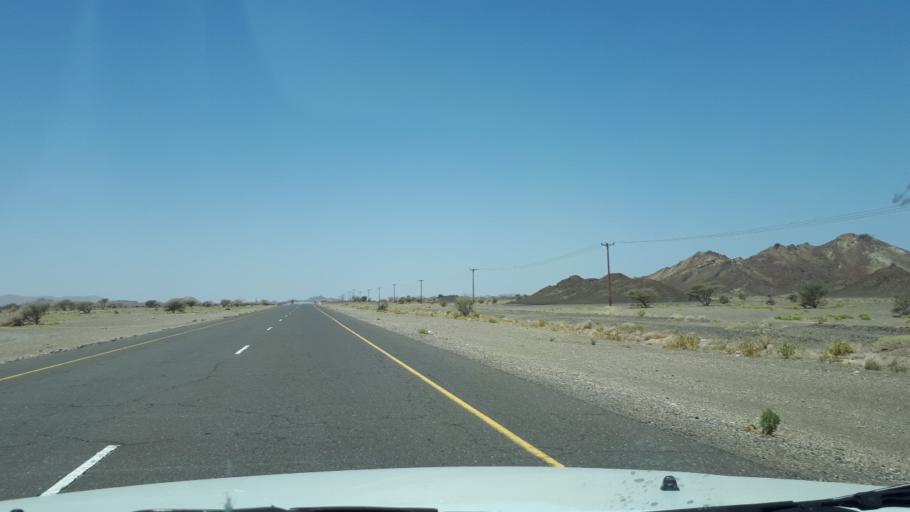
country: OM
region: Ash Sharqiyah
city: Ibra'
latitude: 22.6179
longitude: 58.4358
